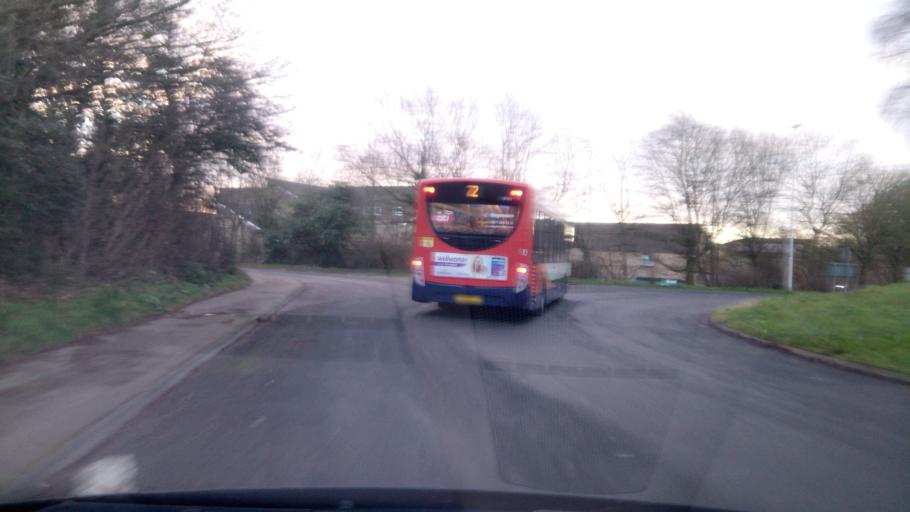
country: GB
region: England
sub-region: Peterborough
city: Marholm
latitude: 52.5826
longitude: -0.2881
